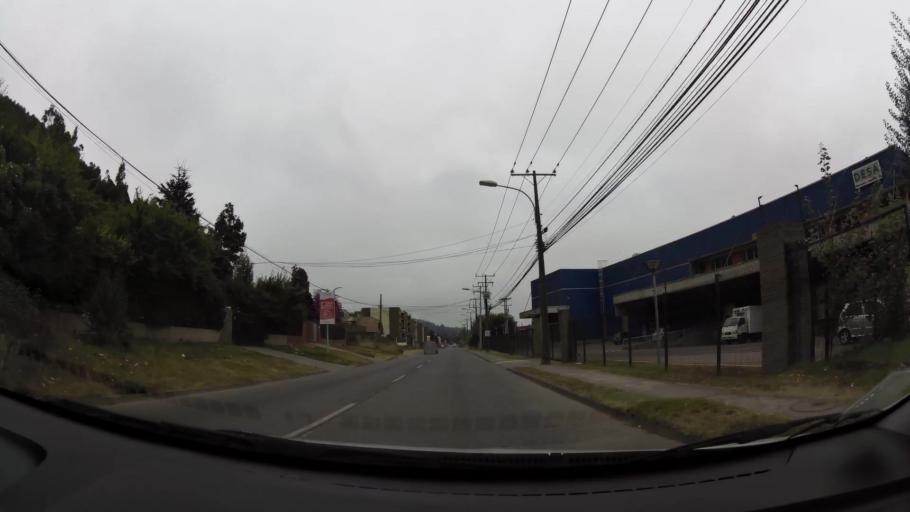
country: CL
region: Biobio
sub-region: Provincia de Concepcion
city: Concepcion
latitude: -36.8222
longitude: -73.0011
